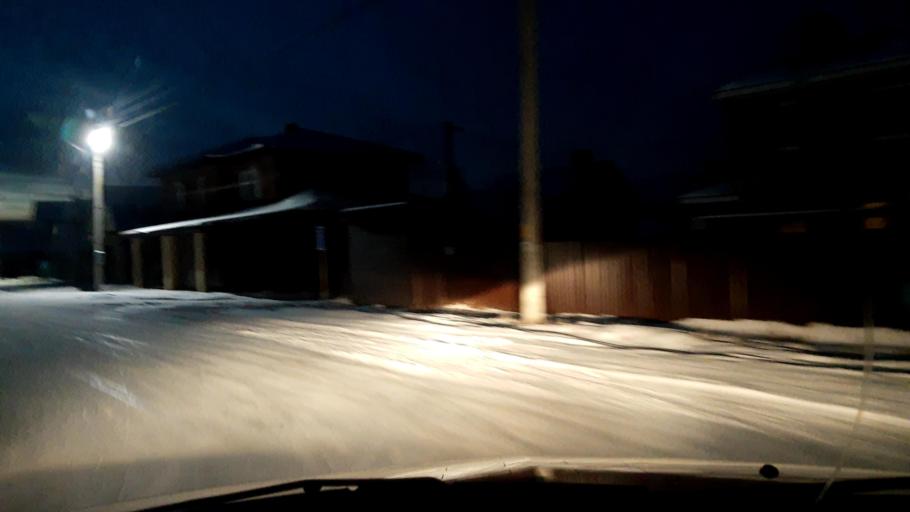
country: RU
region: Bashkortostan
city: Ufa
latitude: 54.6158
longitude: 55.9484
